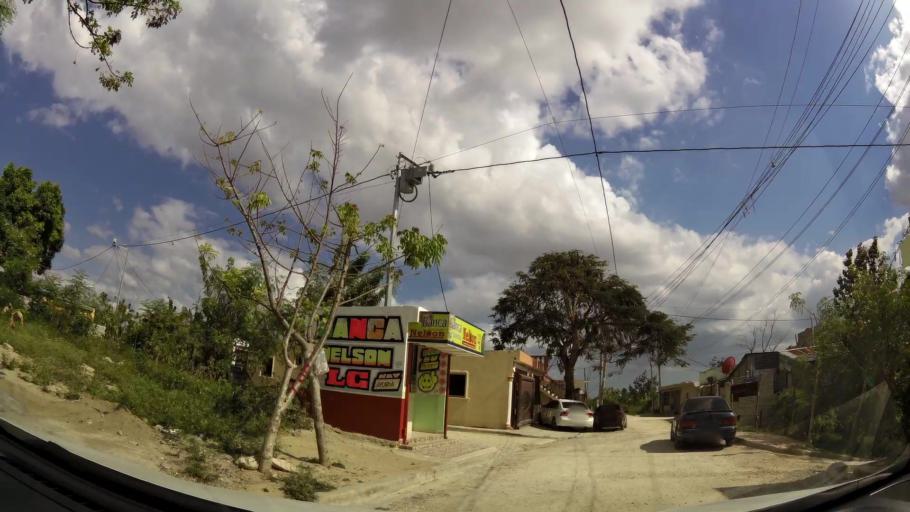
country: DO
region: Nacional
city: Ensanche Luperon
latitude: 18.5293
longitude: -69.8916
